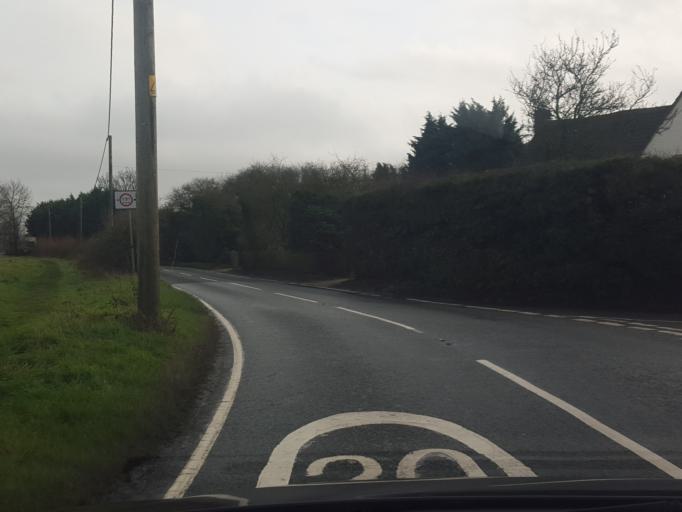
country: GB
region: England
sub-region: Essex
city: Eight Ash Green
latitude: 51.9500
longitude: 0.8040
